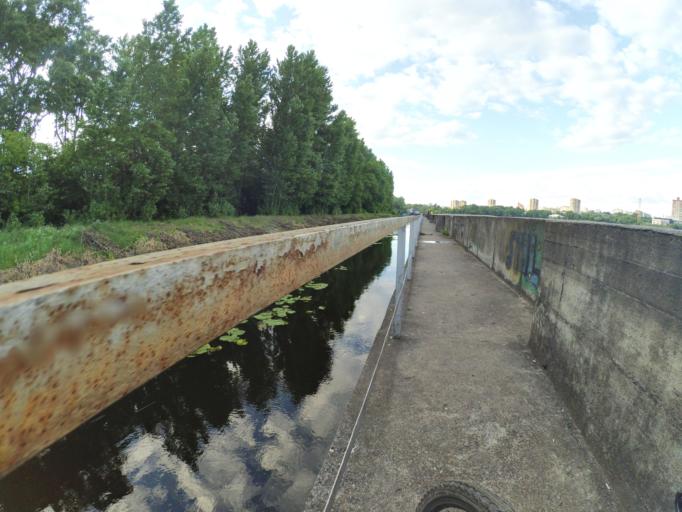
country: RU
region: Moskovskaya
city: Levoberezhnyy
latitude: 55.8390
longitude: 37.4664
